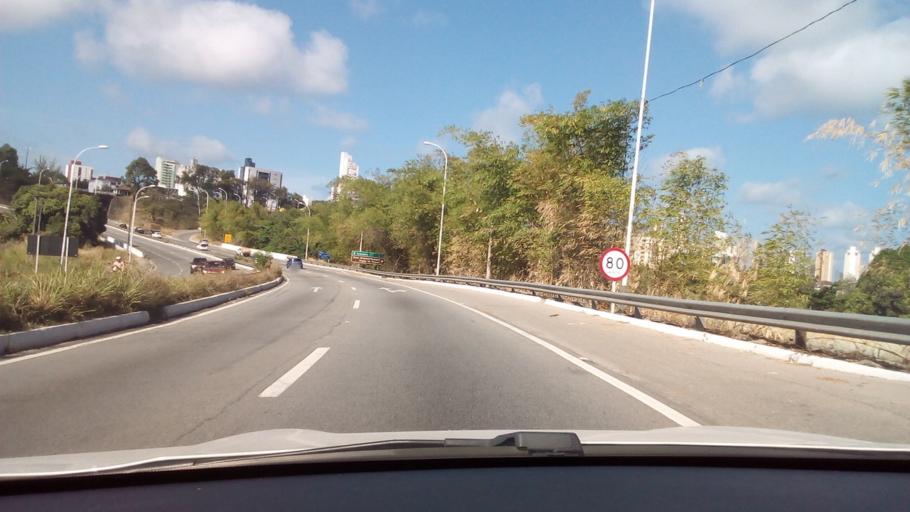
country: BR
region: Paraiba
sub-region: Joao Pessoa
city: Joao Pessoa
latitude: -7.1279
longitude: -34.8461
